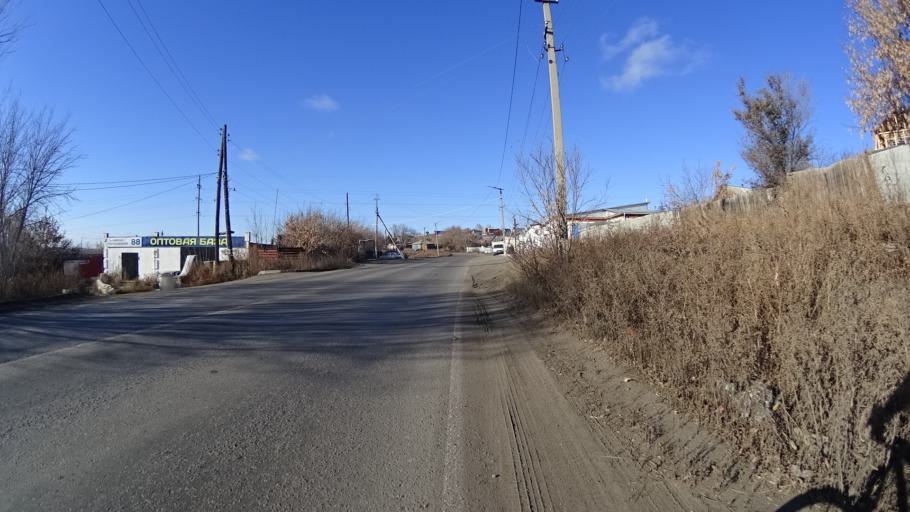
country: RU
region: Chelyabinsk
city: Troitsk
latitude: 54.0971
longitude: 61.5514
